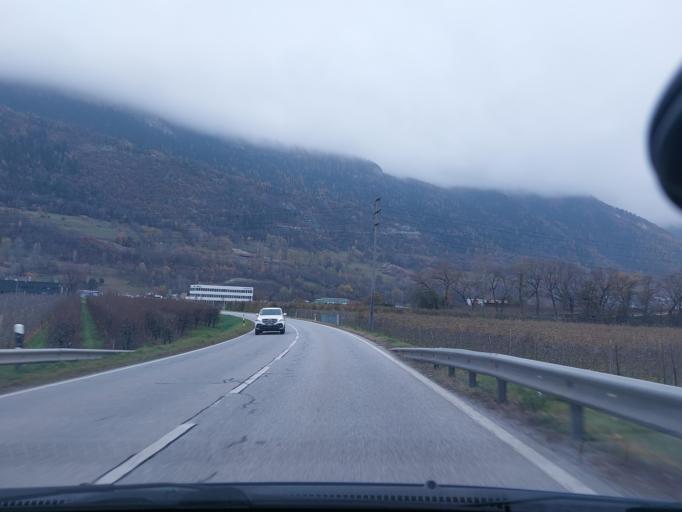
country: CH
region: Valais
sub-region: Sierre District
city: Chalais
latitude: 46.2761
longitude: 7.5160
